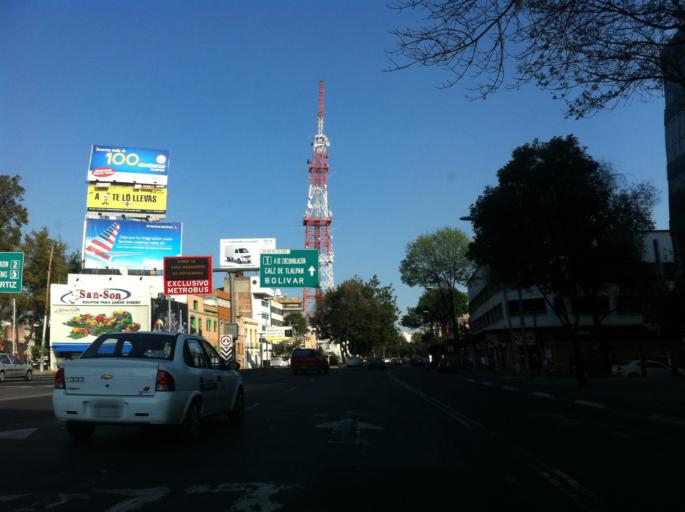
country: MX
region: Mexico City
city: Cuauhtemoc
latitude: 19.4257
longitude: -99.1533
